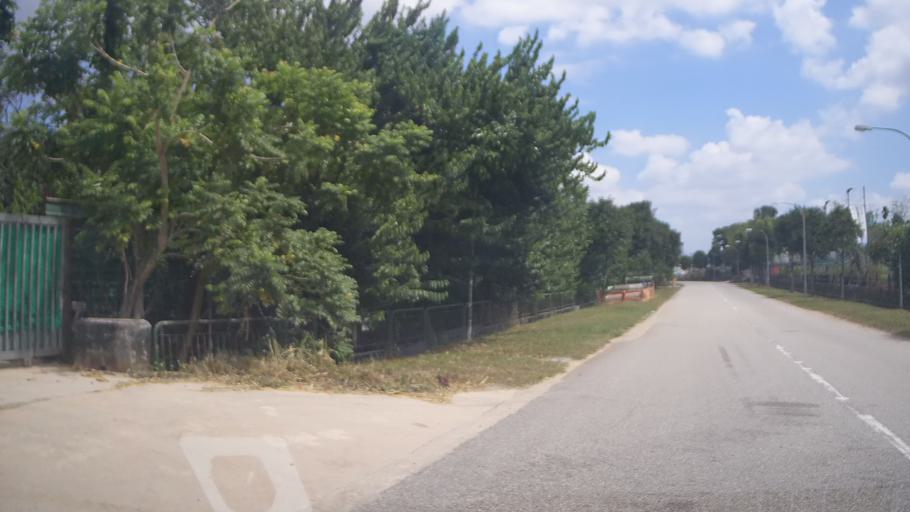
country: MY
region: Johor
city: Johor Bahru
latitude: 1.4399
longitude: 103.7274
